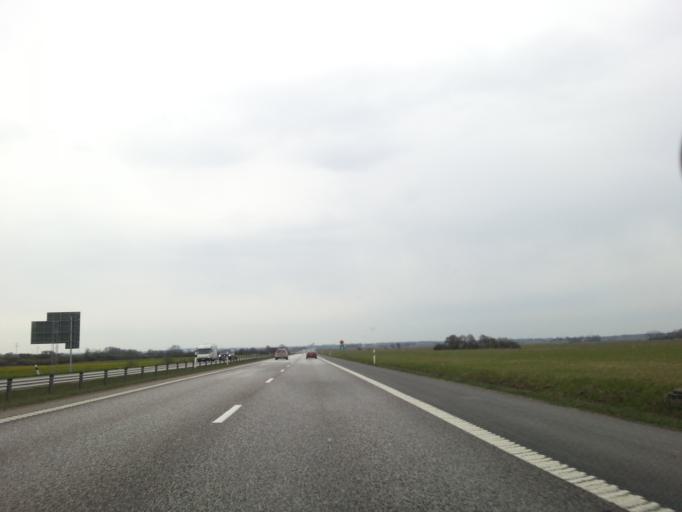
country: SE
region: Skane
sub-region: Angelholms Kommun
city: AEngelholm
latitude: 56.3074
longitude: 12.9090
